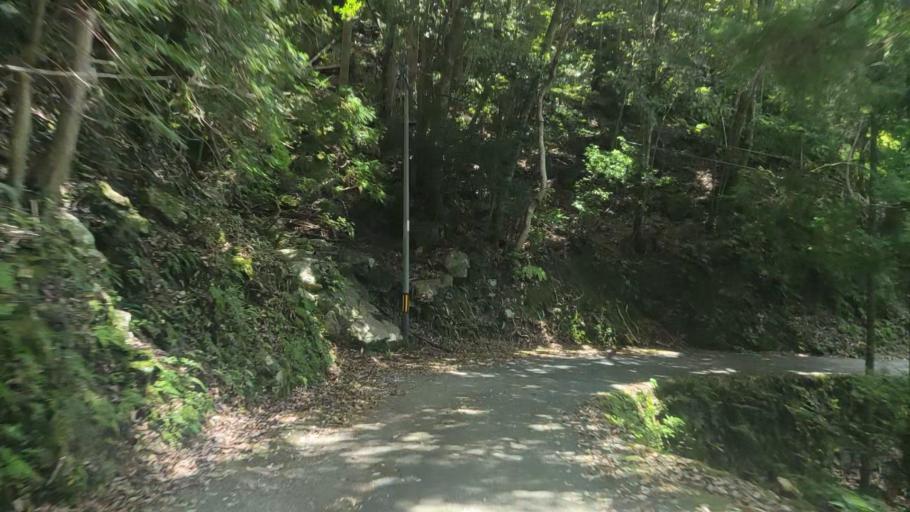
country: JP
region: Wakayama
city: Shingu
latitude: 33.9076
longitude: 135.8656
